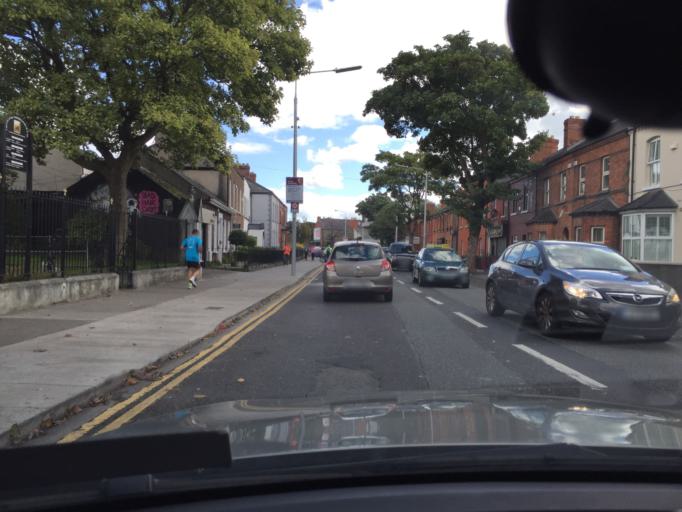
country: IE
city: Fairview
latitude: 53.3628
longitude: -6.2394
